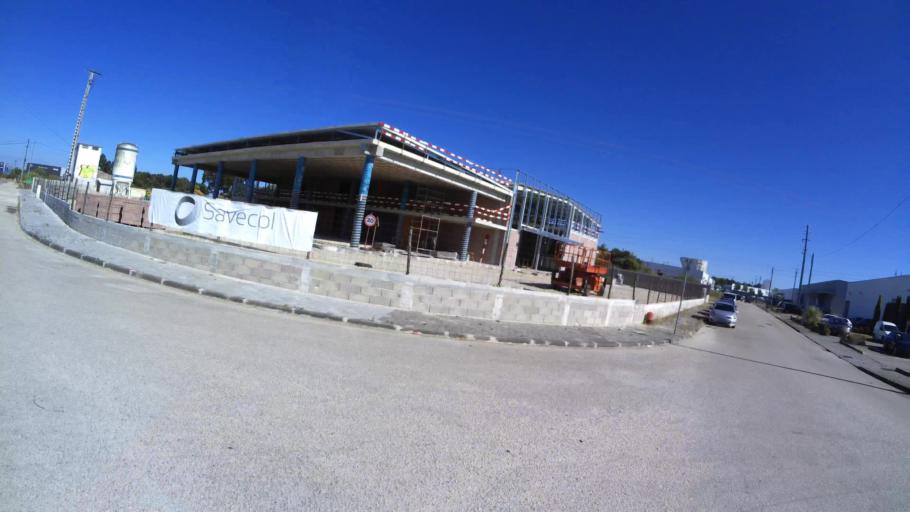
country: PT
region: Aveiro
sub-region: Aveiro
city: Aveiro
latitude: 40.6509
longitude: -8.6066
